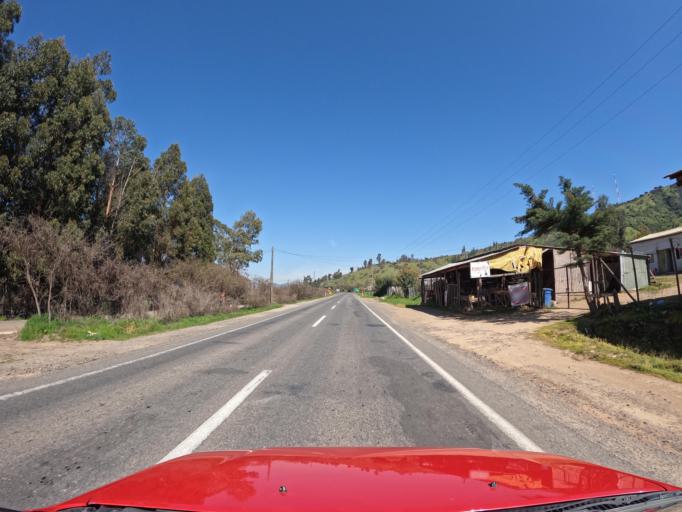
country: CL
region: Maule
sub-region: Provincia de Talca
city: Talca
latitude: -35.0836
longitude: -71.6412
